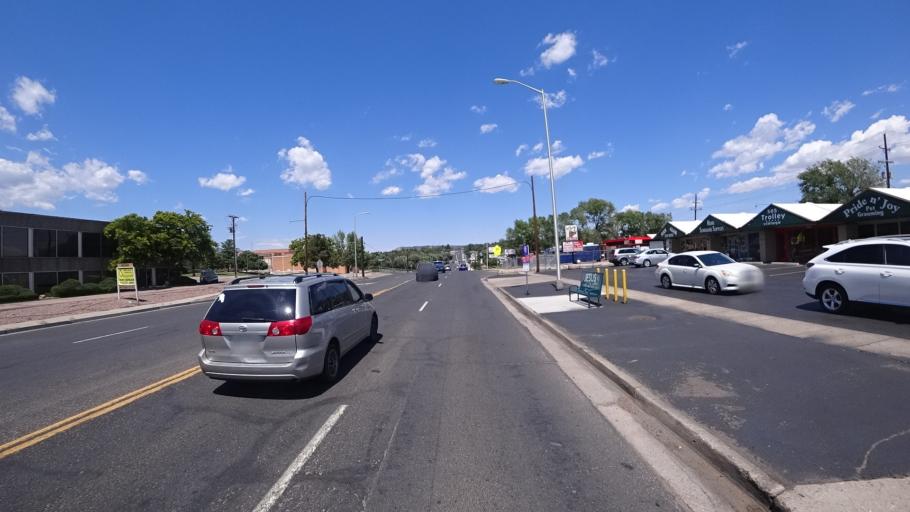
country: US
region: Colorado
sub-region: El Paso County
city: Colorado Springs
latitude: 38.8548
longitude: -104.7942
